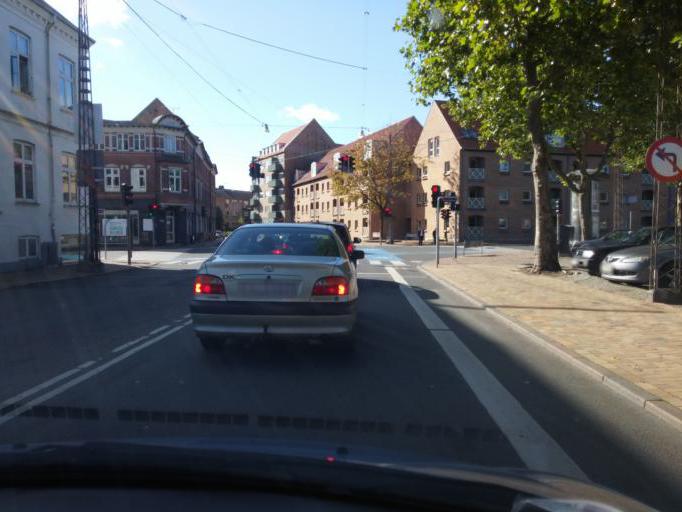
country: DK
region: South Denmark
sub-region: Odense Kommune
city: Odense
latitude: 55.3943
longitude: 10.3768
